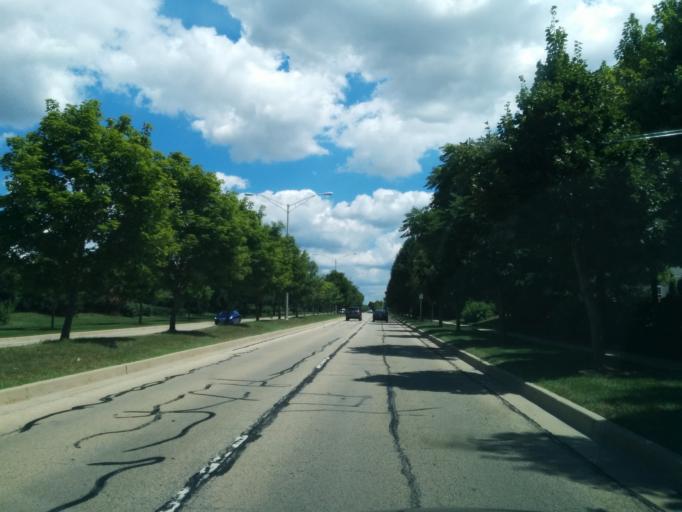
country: US
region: Illinois
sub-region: Will County
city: Romeoville
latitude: 41.6820
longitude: -88.1404
